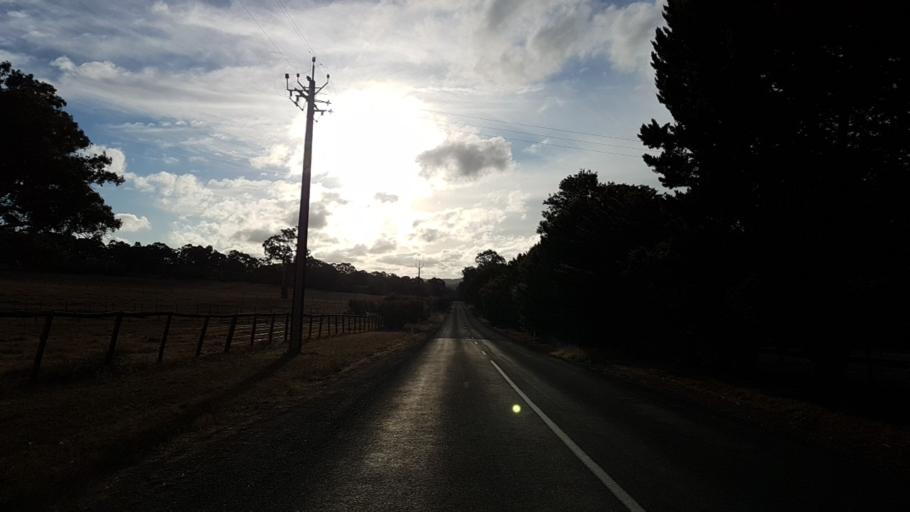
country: AU
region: South Australia
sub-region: Adelaide Hills
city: Oakbank
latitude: -34.9764
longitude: 138.8677
